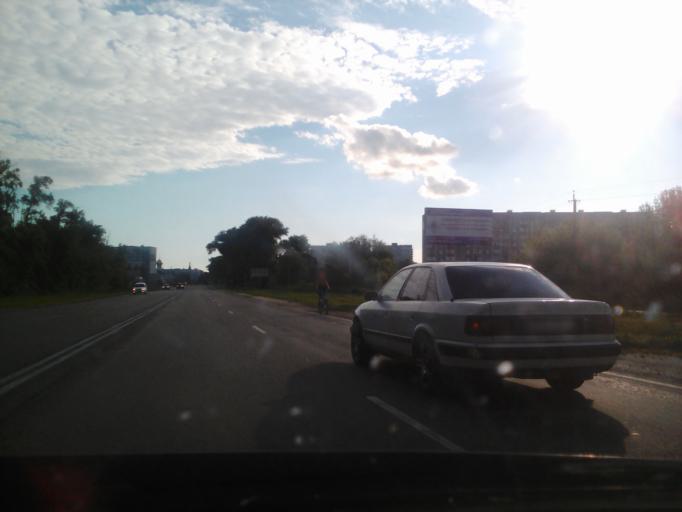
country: RU
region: Kursk
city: Kurchatov
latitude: 51.6571
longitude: 35.7041
